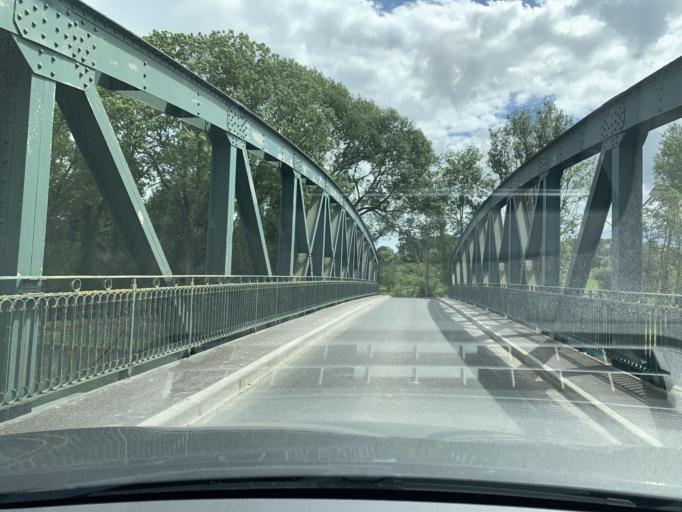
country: FR
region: Nord-Pas-de-Calais
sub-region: Departement du Nord
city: Masnieres
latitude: 50.0775
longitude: 3.2172
